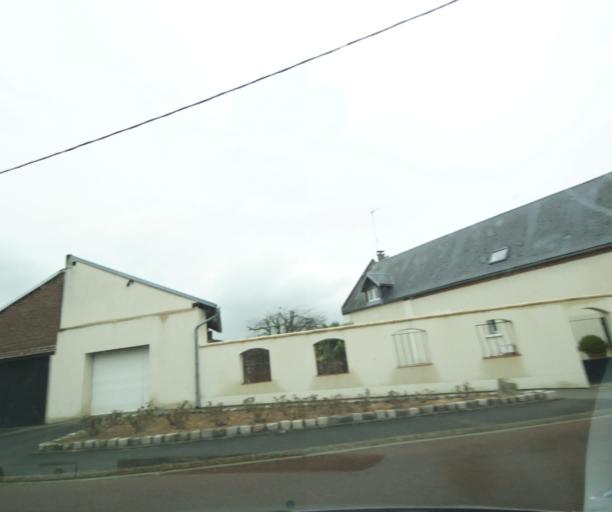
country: FR
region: Picardie
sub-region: Departement de l'Oise
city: Noyon
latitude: 49.5696
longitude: 3.0329
